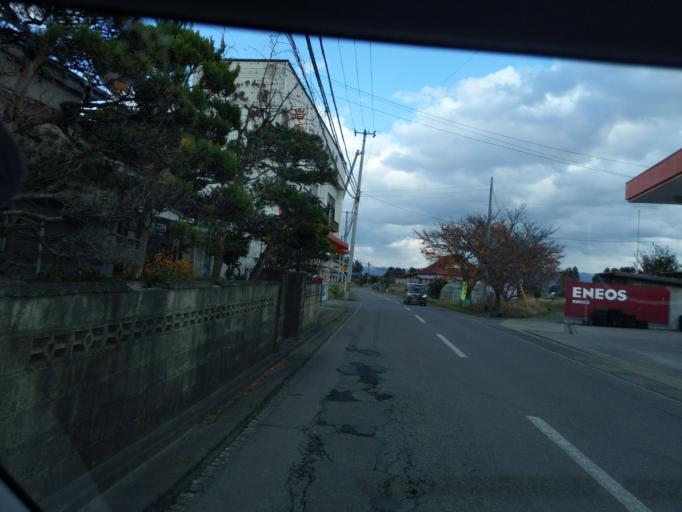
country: JP
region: Iwate
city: Mizusawa
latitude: 39.1286
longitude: 141.0959
